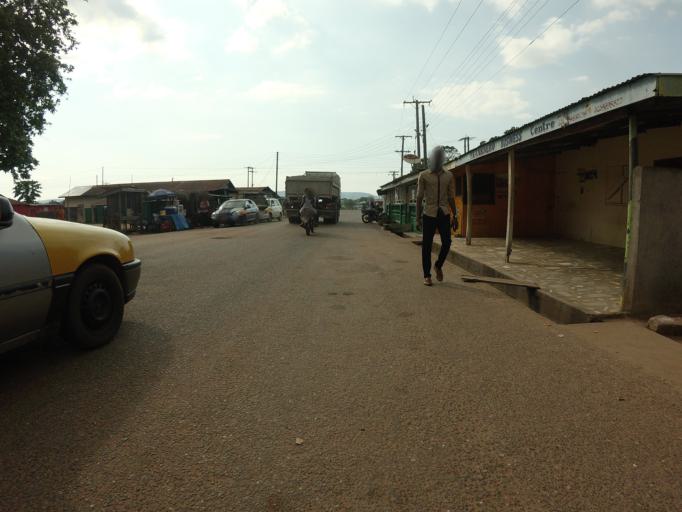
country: GH
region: Volta
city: Ho
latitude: 6.5698
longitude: 0.4013
